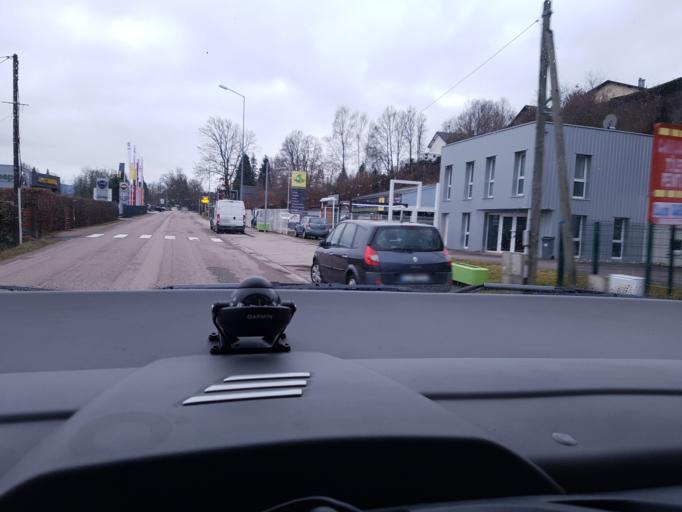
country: FR
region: Lorraine
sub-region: Departement des Vosges
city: Saint-Die-des-Vosges
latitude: 48.2697
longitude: 6.9615
